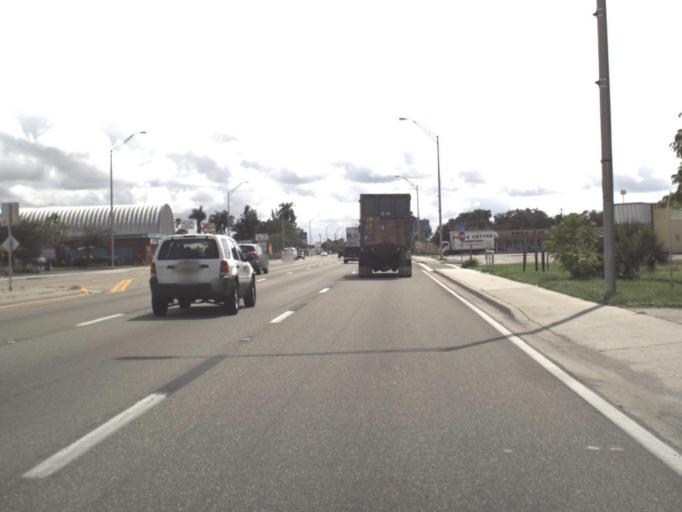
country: US
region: Florida
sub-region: Lee County
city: North Fort Myers
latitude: 26.6659
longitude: -81.8795
